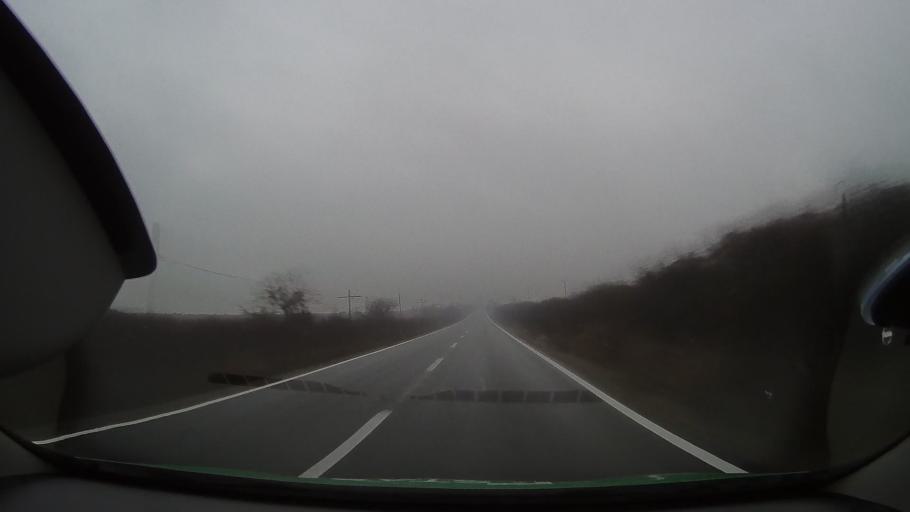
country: RO
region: Bihor
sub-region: Comuna Olcea
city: Calacea
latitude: 46.7211
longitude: 21.9498
